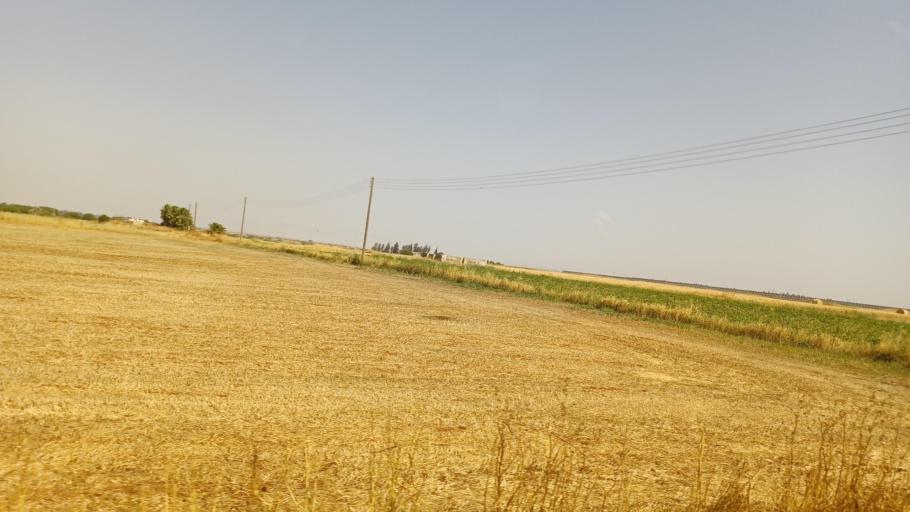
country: CY
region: Ammochostos
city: Avgorou
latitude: 35.0569
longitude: 33.8566
